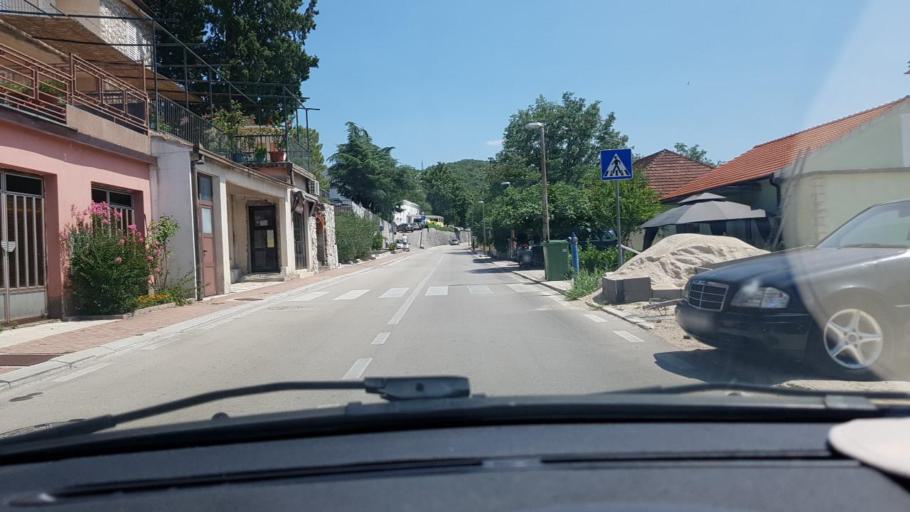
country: HR
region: Splitsko-Dalmatinska
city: Vrgorac
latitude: 43.2029
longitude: 17.3738
